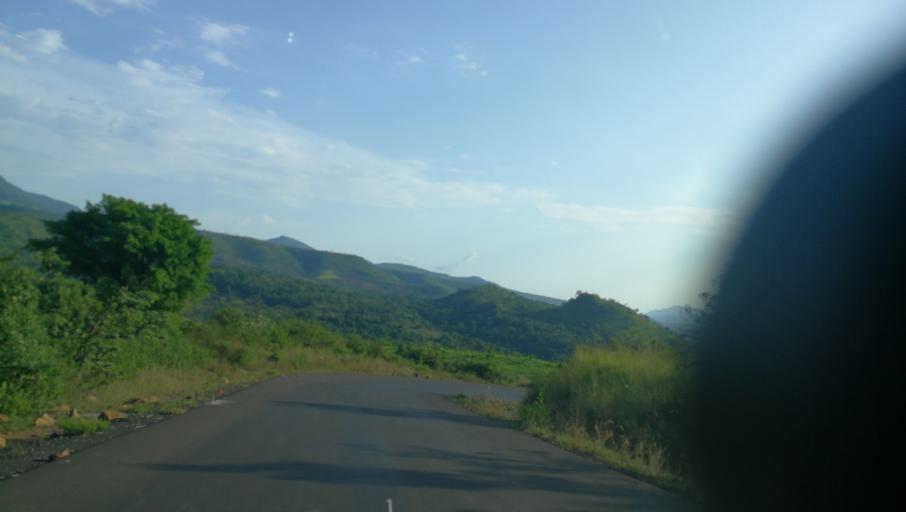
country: ET
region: Southern Nations, Nationalities, and People's Region
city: Areka
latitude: 6.8255
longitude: 37.3009
